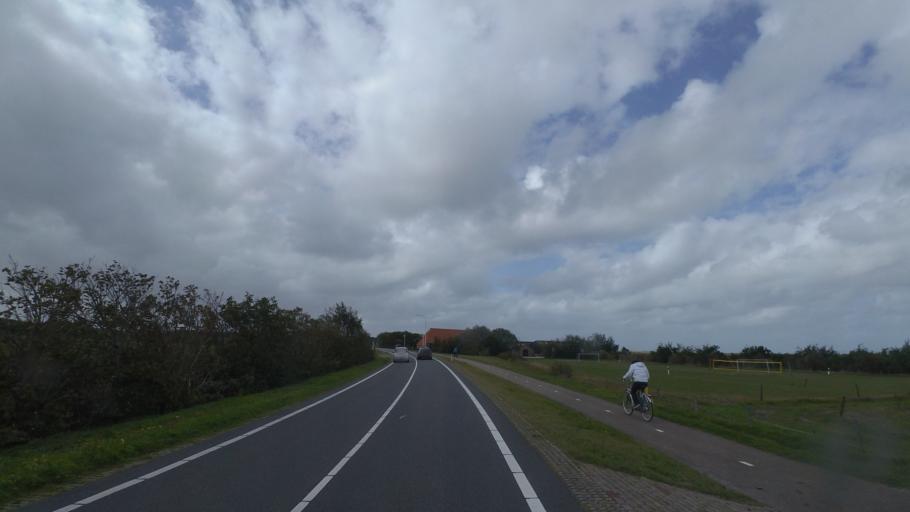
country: NL
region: Friesland
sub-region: Gemeente Ameland
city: Hollum
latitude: 53.4470
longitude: 5.6715
